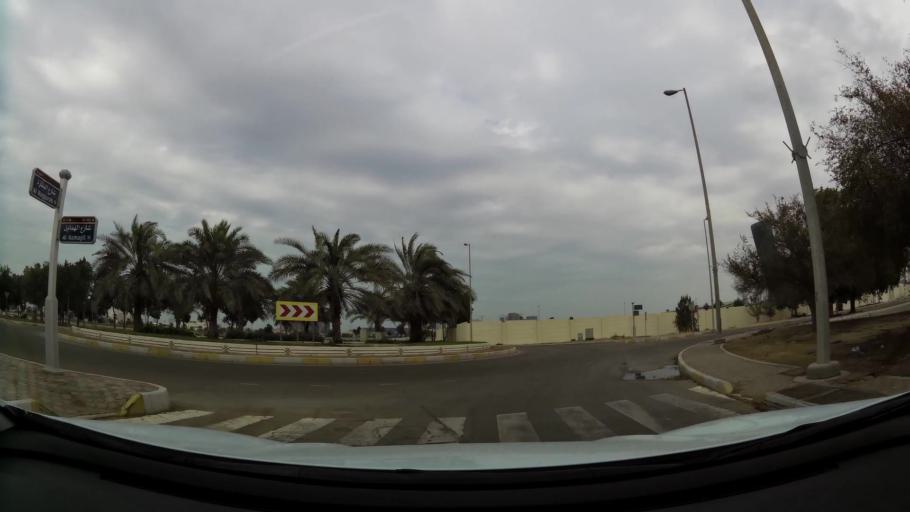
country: AE
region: Abu Dhabi
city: Abu Dhabi
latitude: 24.4157
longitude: 54.4271
